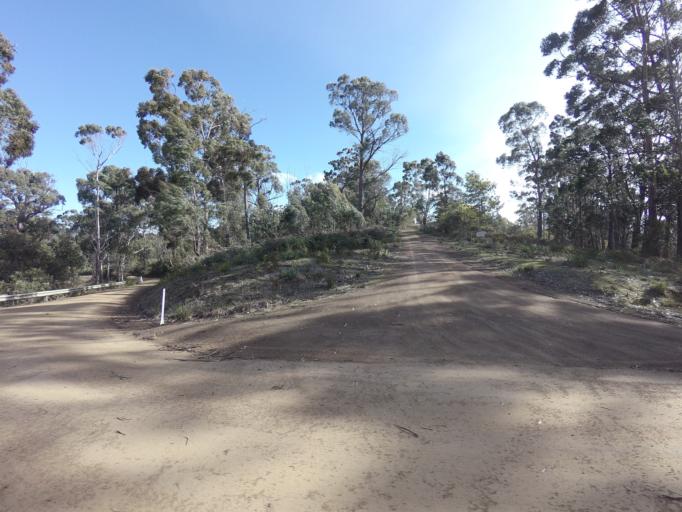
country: AU
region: Tasmania
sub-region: Kingborough
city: Kettering
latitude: -43.0911
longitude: 147.2669
